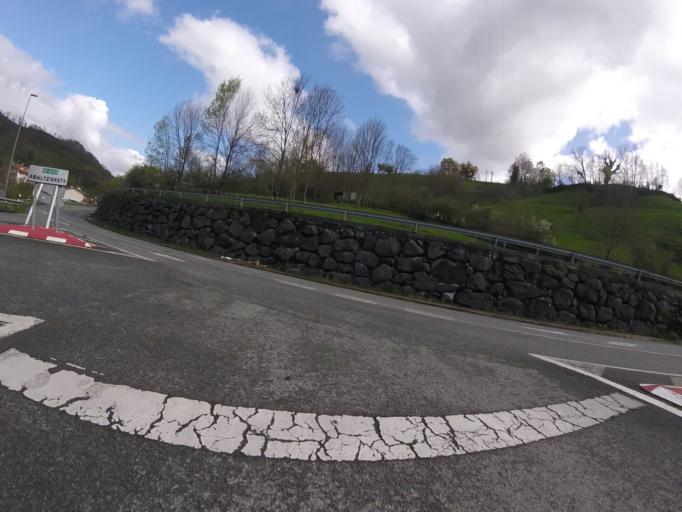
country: ES
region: Basque Country
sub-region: Provincia de Guipuzcoa
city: Amezqueta
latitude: 43.0505
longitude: -2.0882
